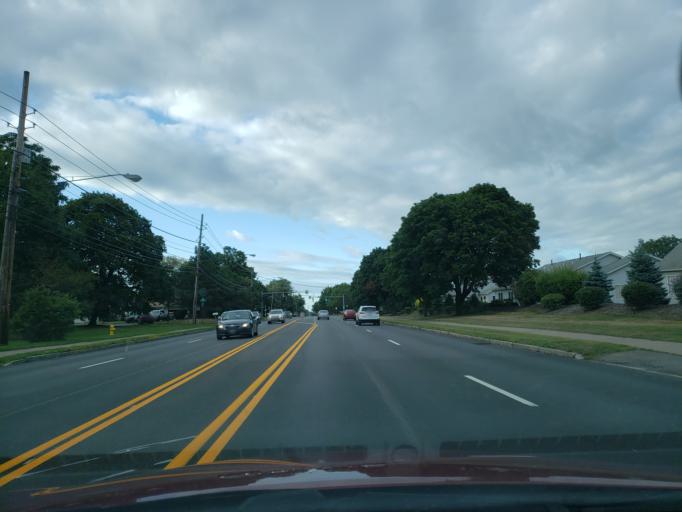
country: US
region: New York
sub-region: Monroe County
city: Greece
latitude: 43.2297
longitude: -77.6591
